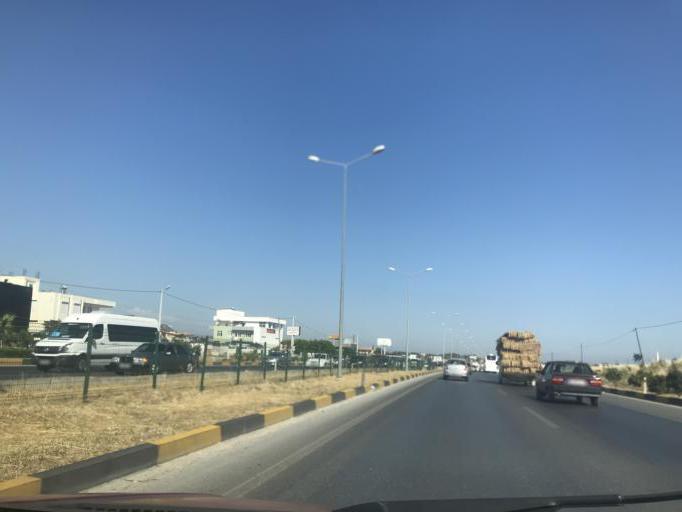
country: TR
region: Antalya
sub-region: Manavgat
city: Side
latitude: 36.8044
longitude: 31.3925
